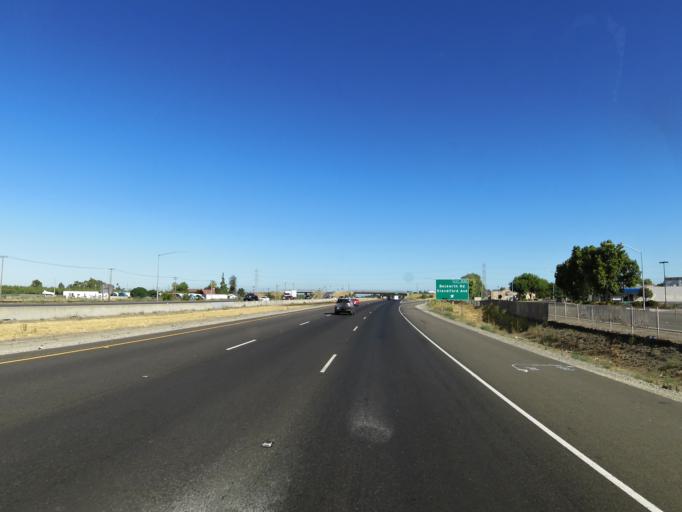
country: US
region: California
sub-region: Stanislaus County
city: Salida
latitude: 37.6793
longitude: -121.0485
